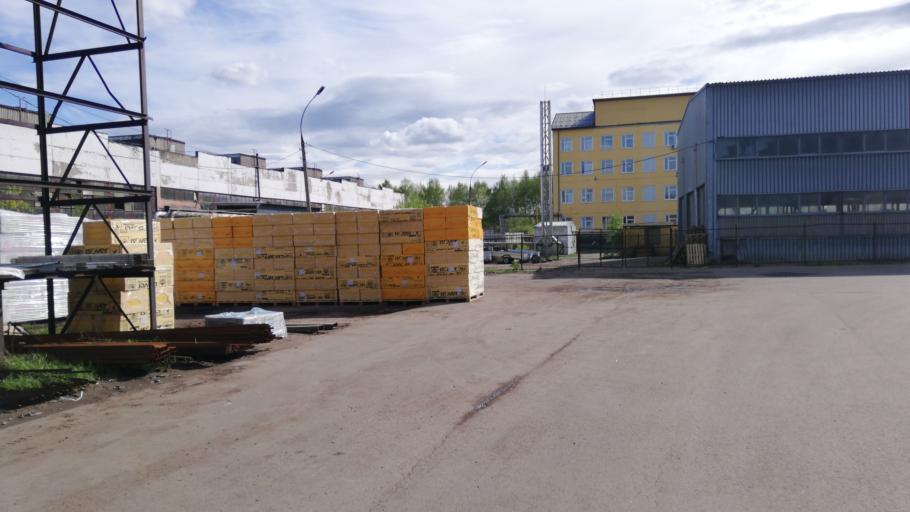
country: RU
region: Jaroslavl
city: Yaroslavl
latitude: 57.6245
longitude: 39.8215
